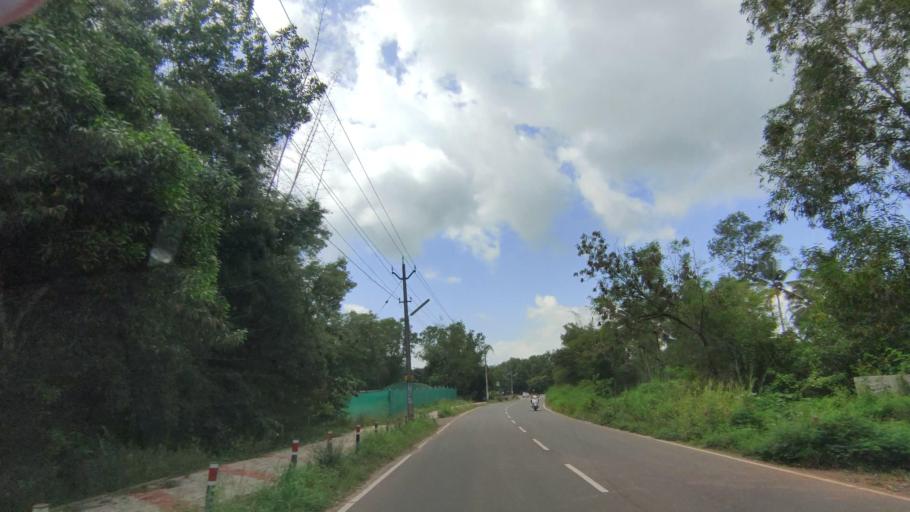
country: IN
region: Kerala
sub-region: Kottayam
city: Kottayam
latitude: 9.5678
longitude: 76.5211
